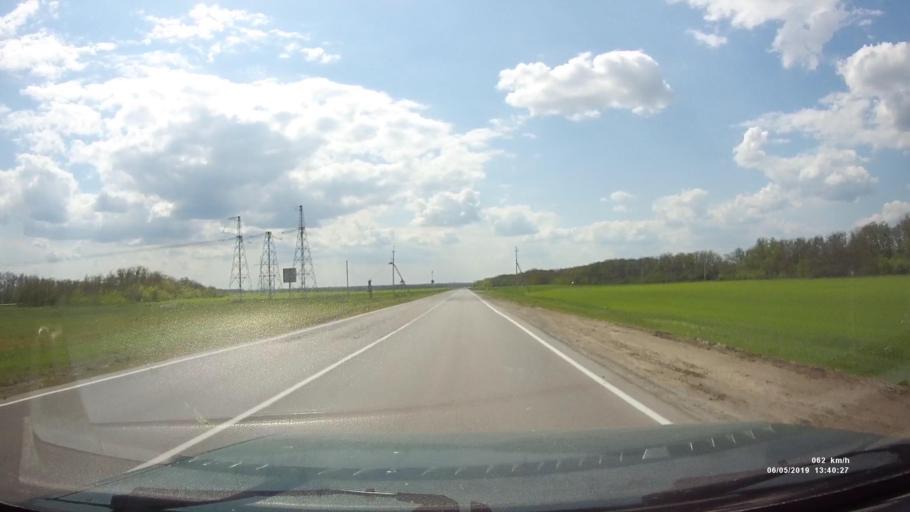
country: RU
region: Rostov
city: Ust'-Donetskiy
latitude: 47.6672
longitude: 40.6935
